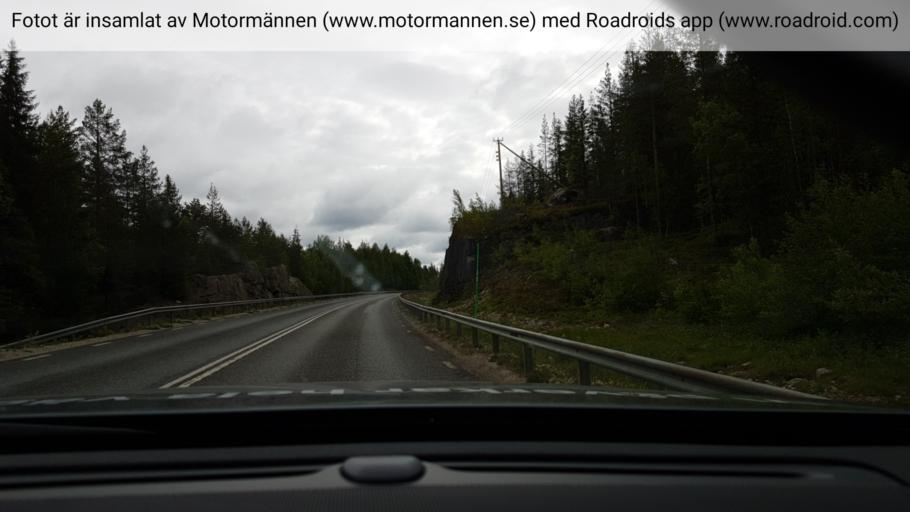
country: SE
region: Vaesterbotten
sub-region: Lycksele Kommun
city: Lycksele
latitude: 64.5724
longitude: 18.6257
